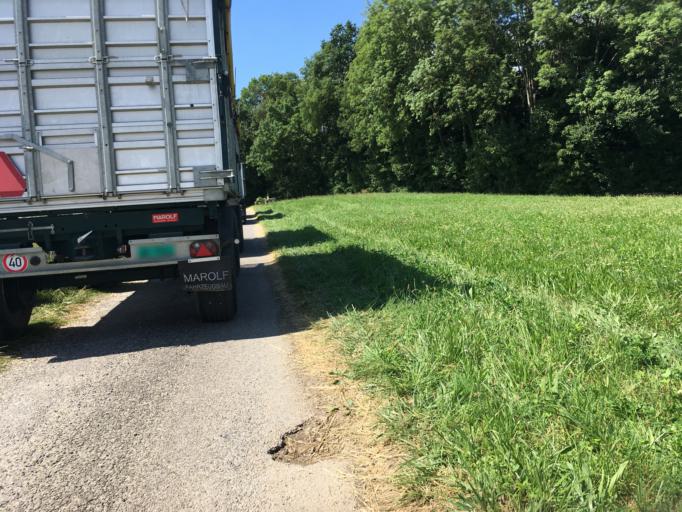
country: CH
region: Neuchatel
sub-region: Neuchatel District
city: Saint-Blaise
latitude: 46.9457
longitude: 7.0041
